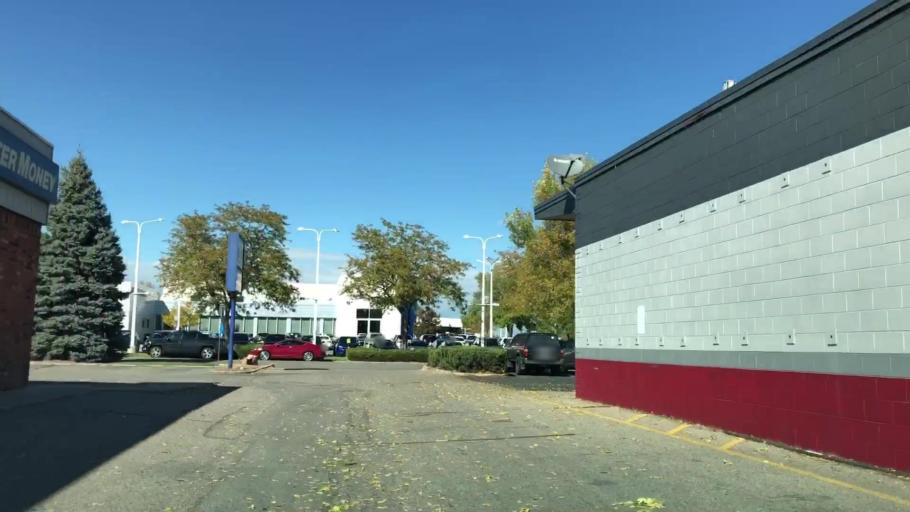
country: US
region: Colorado
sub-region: Larimer County
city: Fort Collins
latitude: 40.5396
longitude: -105.0779
